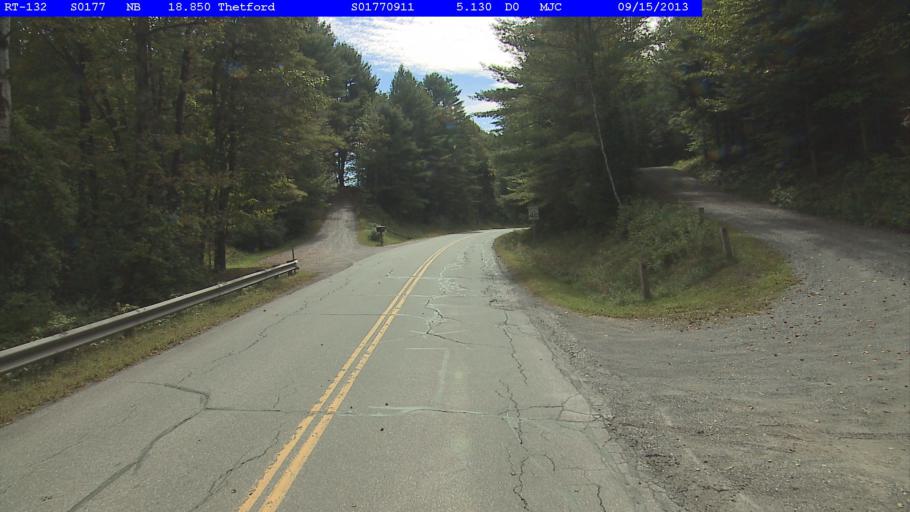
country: US
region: New Hampshire
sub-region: Grafton County
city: Hanover
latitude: 43.7872
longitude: -72.2590
